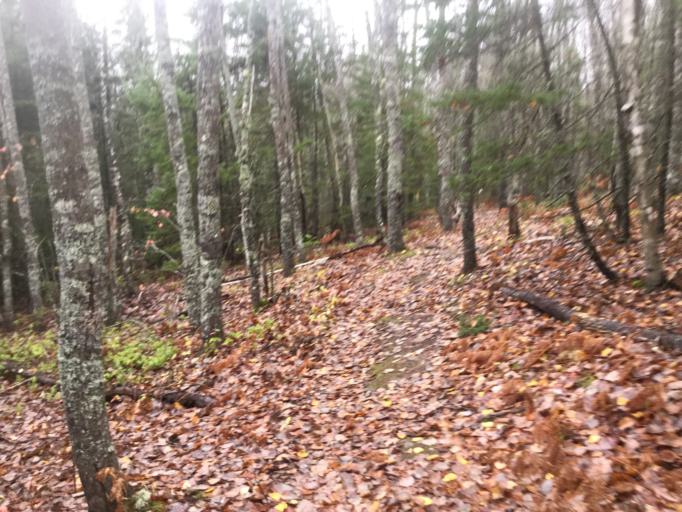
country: CA
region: Nova Scotia
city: New Glasgow
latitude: 45.5498
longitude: -62.6816
